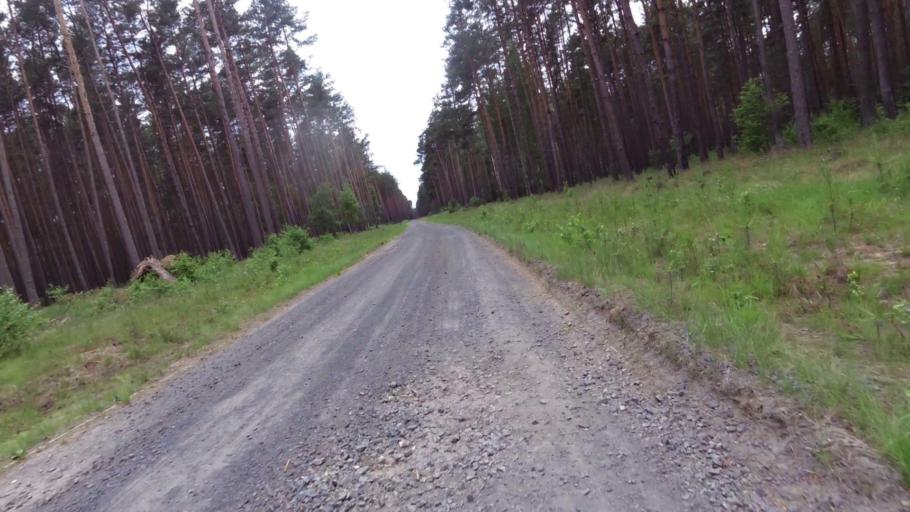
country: PL
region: West Pomeranian Voivodeship
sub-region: Powiat mysliborski
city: Debno
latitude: 52.8321
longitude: 14.6318
